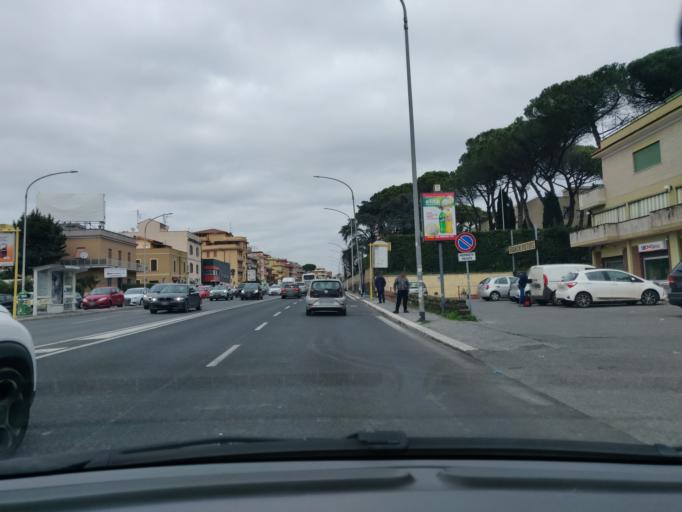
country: VA
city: Vatican City
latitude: 41.8926
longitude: 12.4144
